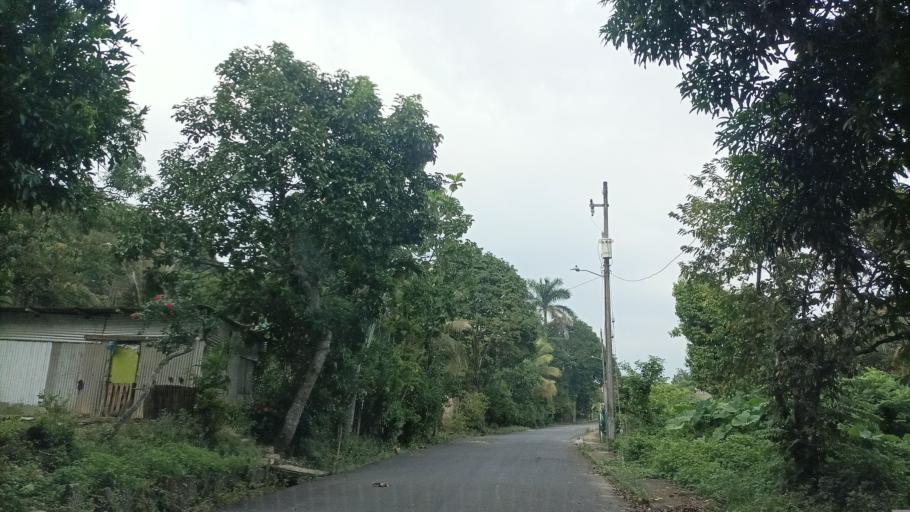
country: MX
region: Veracruz
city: Allende
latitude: 18.1216
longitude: -94.2858
